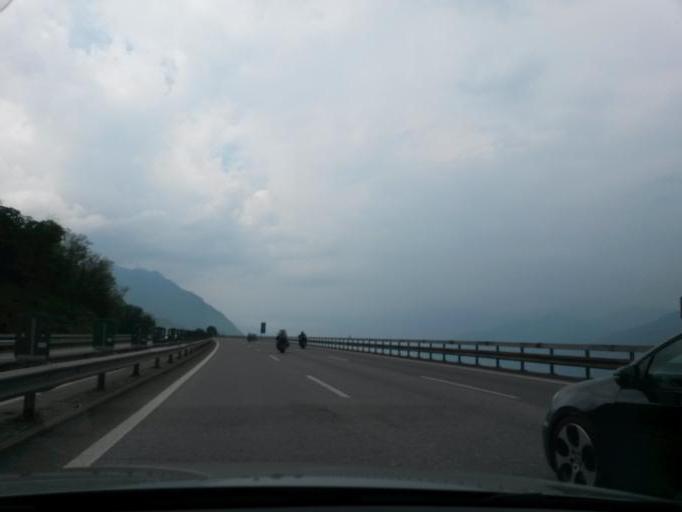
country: CH
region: Ticino
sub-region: Bellinzona District
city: Cadenazzo
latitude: 46.1509
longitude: 8.9681
